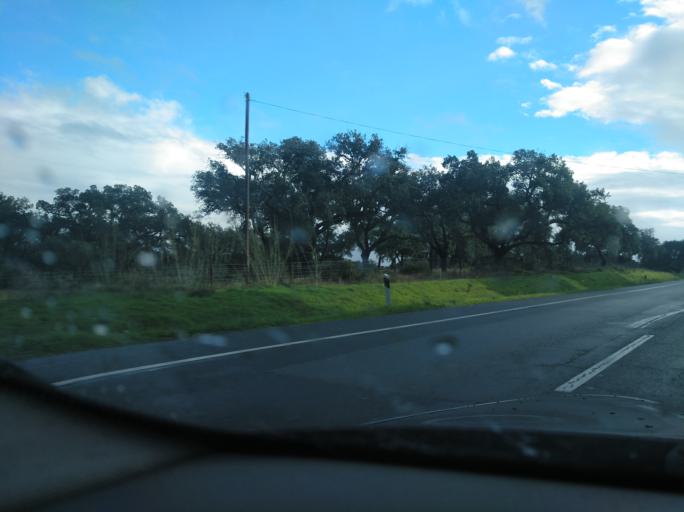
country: PT
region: Setubal
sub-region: Grandola
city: Grandola
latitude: 38.0288
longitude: -8.3999
